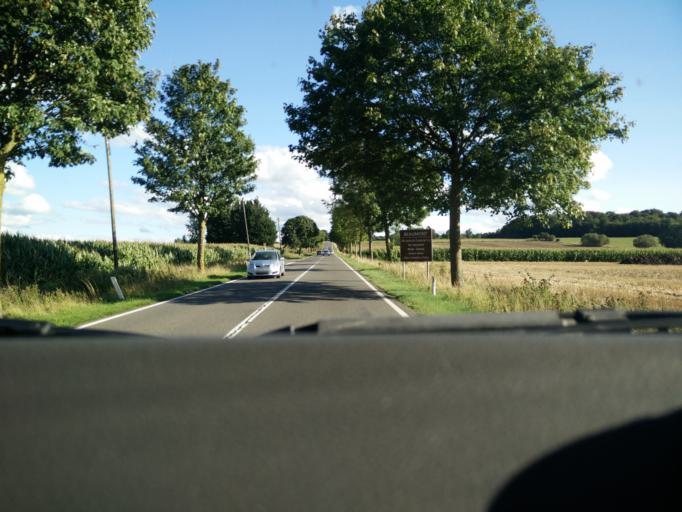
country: BE
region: Wallonia
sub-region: Province du Hainaut
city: Beaumont
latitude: 50.2696
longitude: 4.2142
